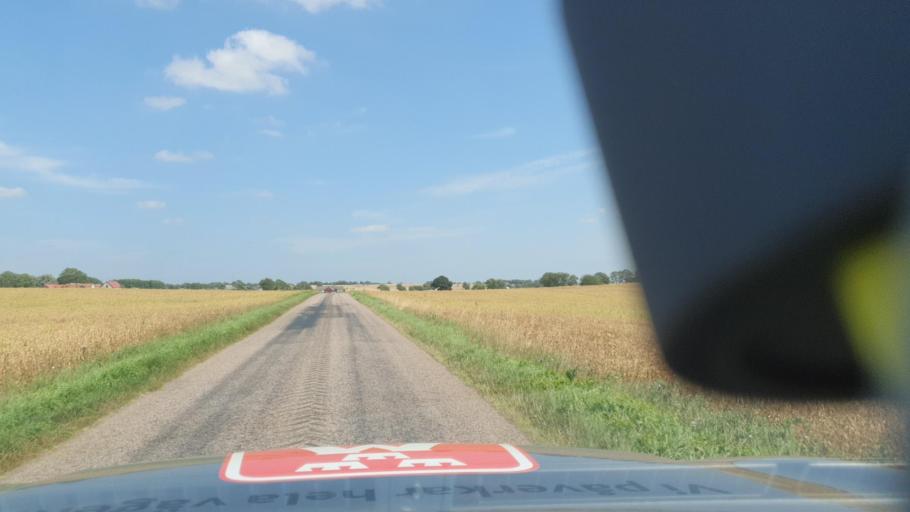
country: SE
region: Skane
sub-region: Tomelilla Kommun
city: Tomelilla
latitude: 55.5808
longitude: 14.0209
